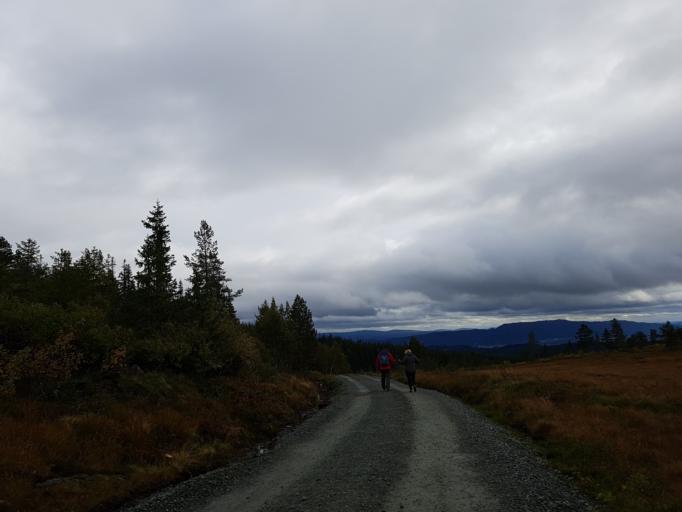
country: NO
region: Sor-Trondelag
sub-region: Melhus
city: Melhus
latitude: 63.4151
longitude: 10.2362
